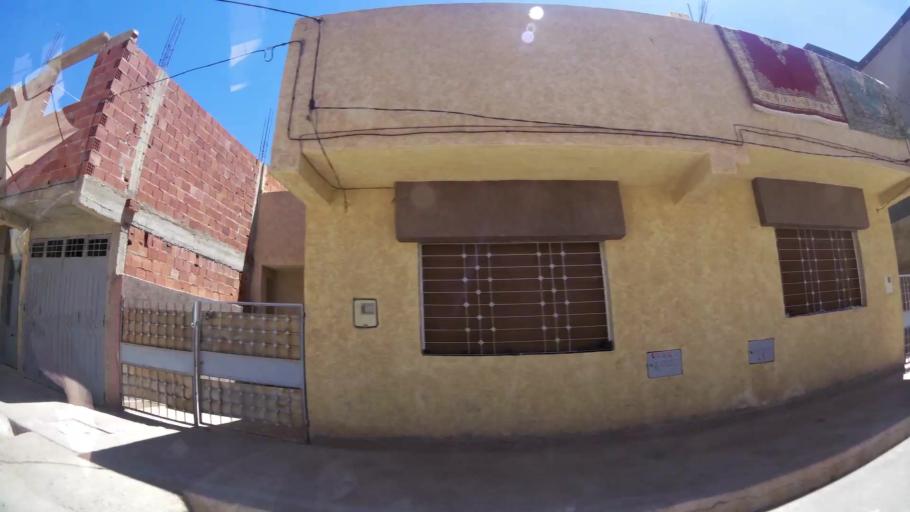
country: MA
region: Oriental
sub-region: Oujda-Angad
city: Oujda
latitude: 34.6802
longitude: -1.8552
